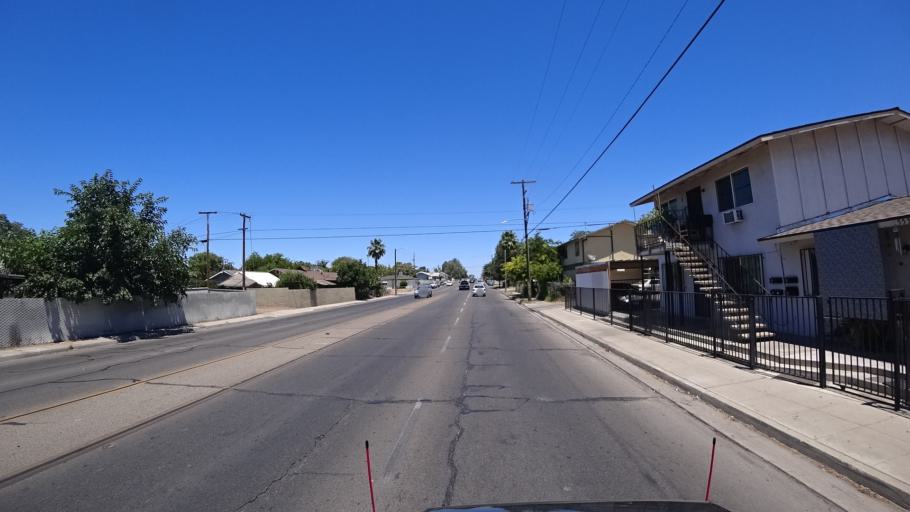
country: US
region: California
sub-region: Fresno County
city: Fresno
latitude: 36.7370
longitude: -119.7455
